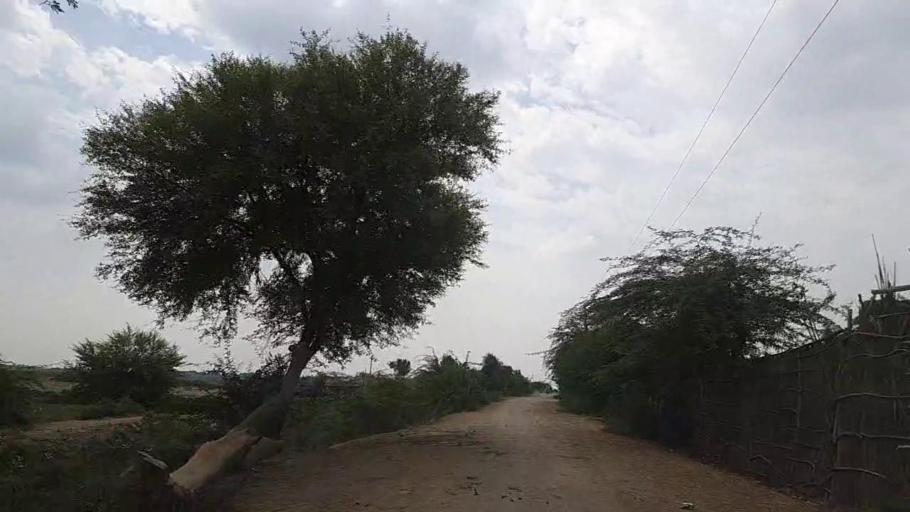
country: PK
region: Sindh
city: Mirpur Batoro
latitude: 24.6229
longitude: 68.1377
